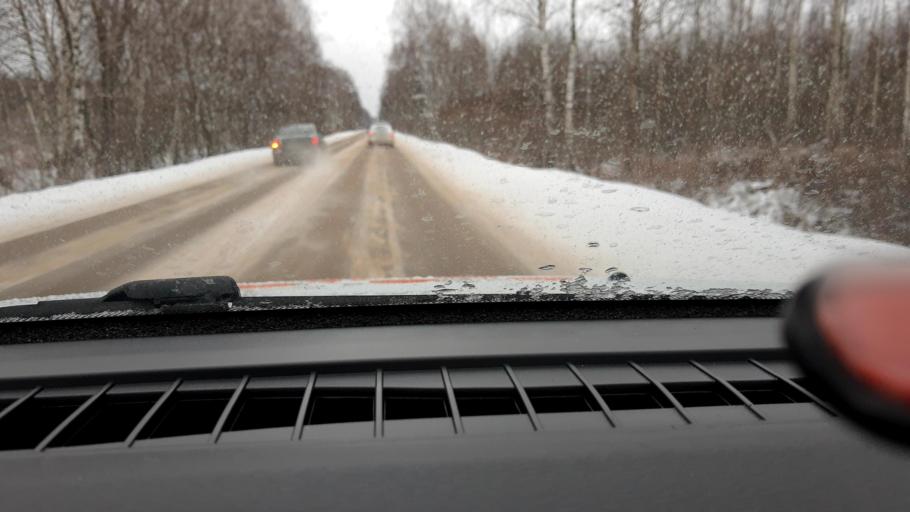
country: RU
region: Nizjnij Novgorod
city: Afonino
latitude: 56.3182
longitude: 44.1804
